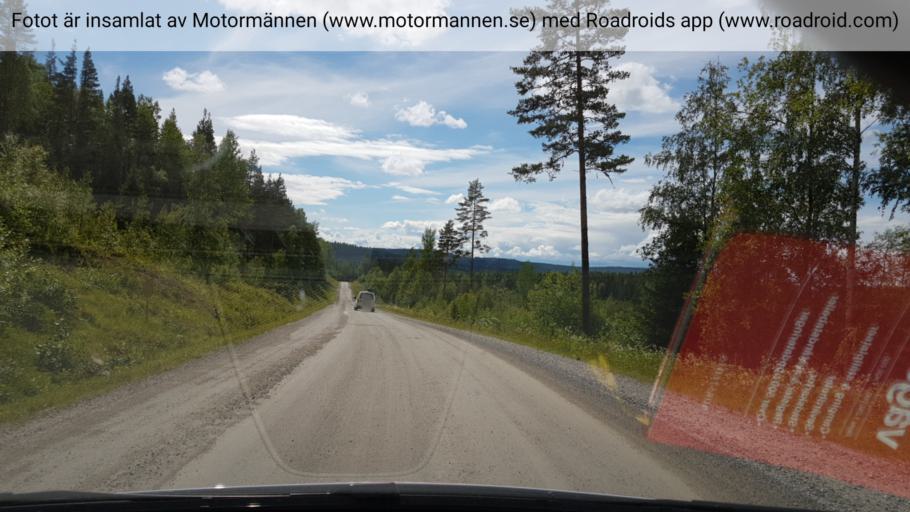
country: SE
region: Vaesternorrland
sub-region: Solleftea Kommun
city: Solleftea
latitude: 63.3186
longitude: 17.2348
